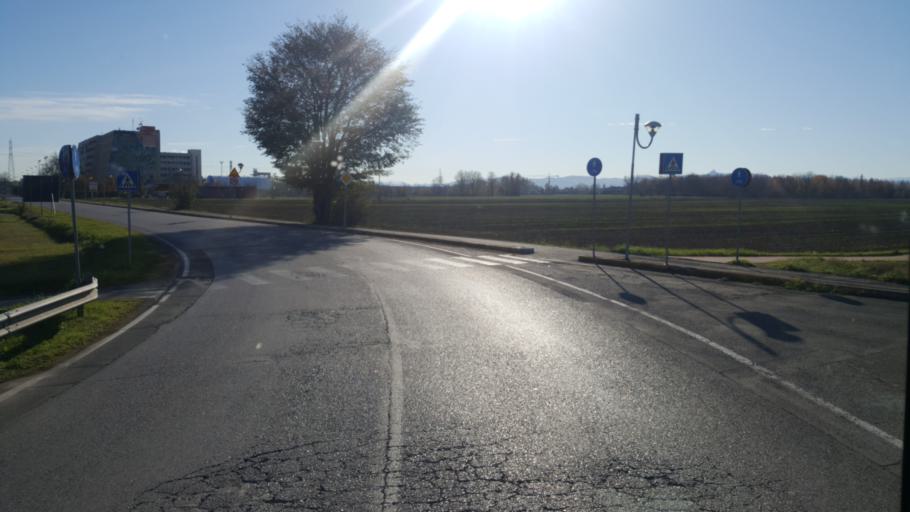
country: IT
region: Emilia-Romagna
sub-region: Provincia di Bologna
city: Calderara di Reno
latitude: 44.5563
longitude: 11.2771
